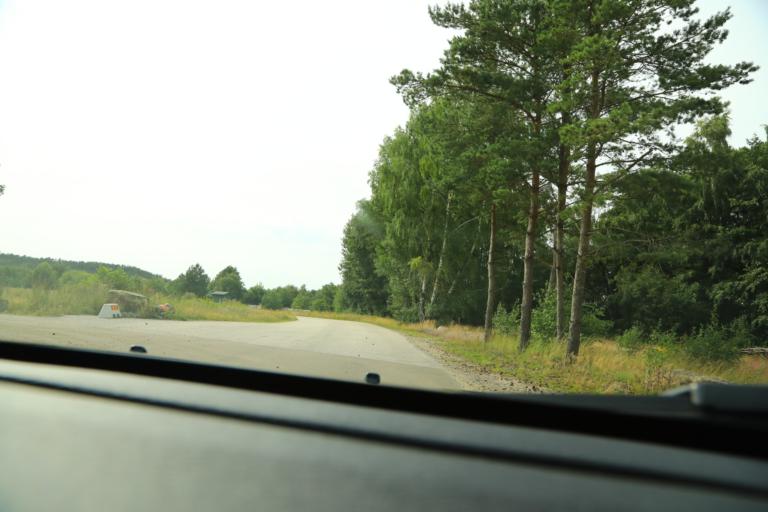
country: SE
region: Halland
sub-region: Varbergs Kommun
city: Varberg
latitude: 57.1835
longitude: 12.2295
